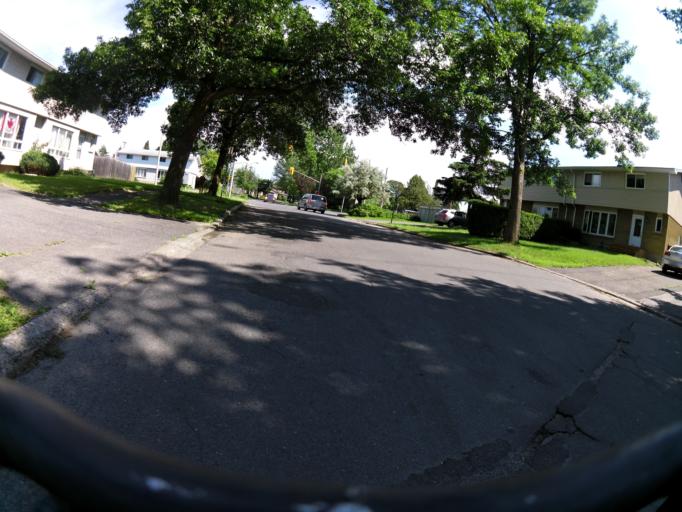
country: CA
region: Ontario
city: Ottawa
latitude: 45.3653
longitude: -75.7074
